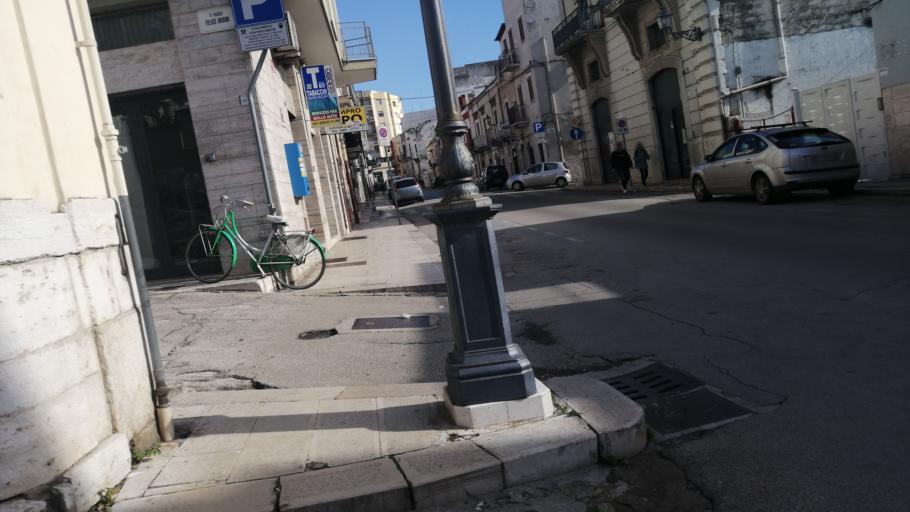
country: IT
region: Apulia
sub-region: Provincia di Barletta - Andria - Trani
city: Andria
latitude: 41.2235
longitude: 16.2966
